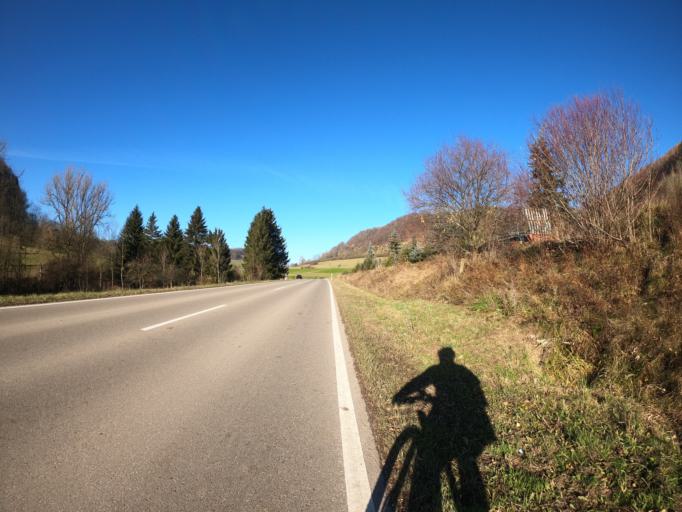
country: DE
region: Baden-Wuerttemberg
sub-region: Regierungsbezirk Stuttgart
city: Eschenbach
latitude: 48.6196
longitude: 9.6792
